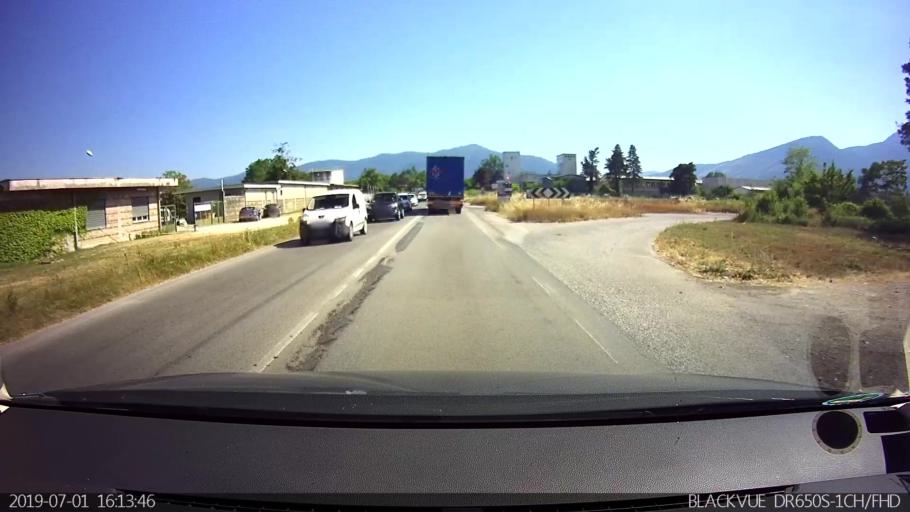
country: IT
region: Latium
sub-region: Provincia di Frosinone
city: Ceccano
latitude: 41.6053
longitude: 13.3001
